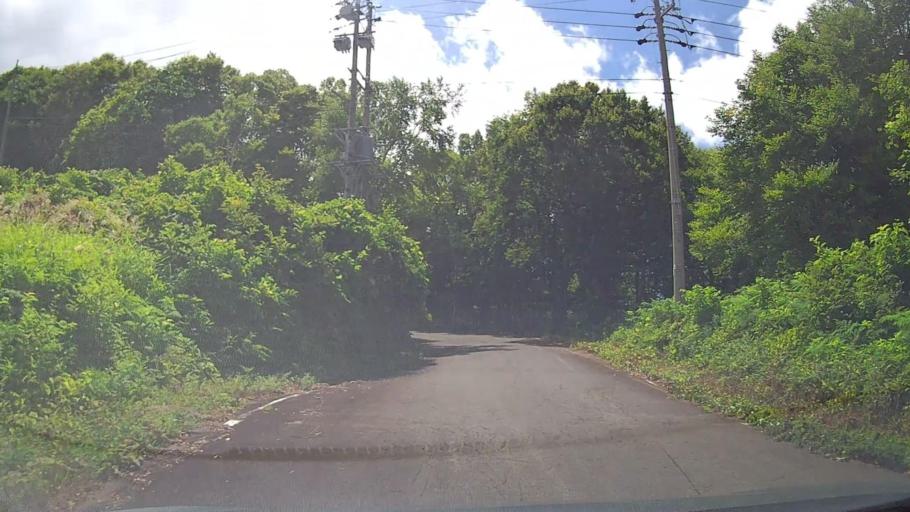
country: JP
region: Nagano
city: Iiyama
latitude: 36.9225
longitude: 138.4753
